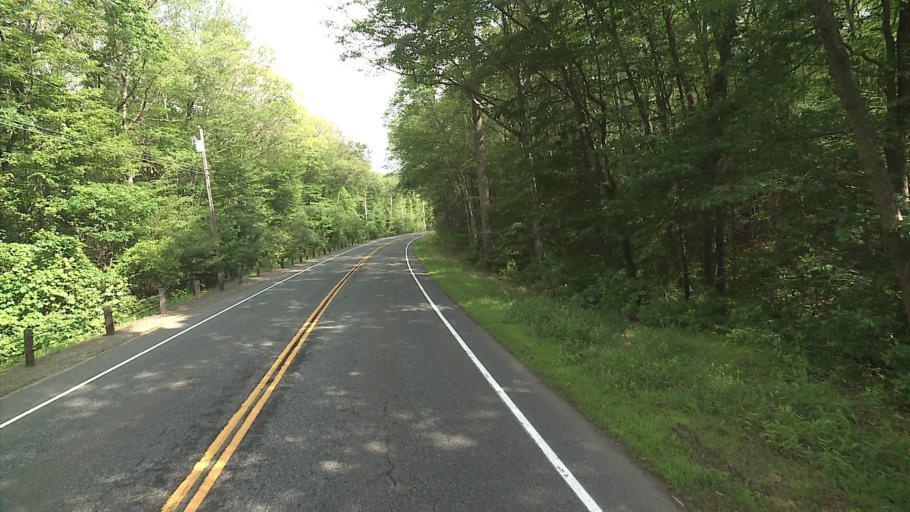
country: US
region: Connecticut
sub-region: Middlesex County
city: Chester Center
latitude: 41.3800
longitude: -72.5089
